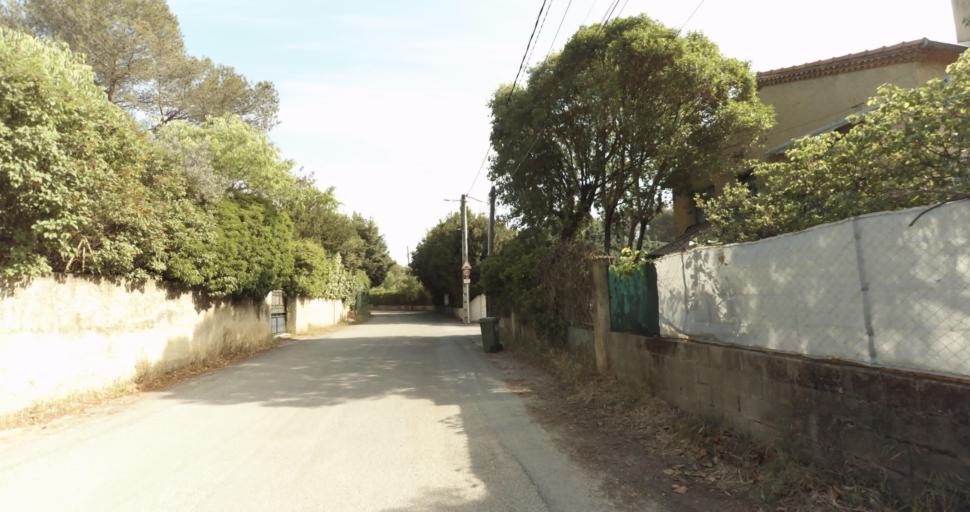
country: FR
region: Languedoc-Roussillon
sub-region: Departement du Gard
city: Nimes
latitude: 43.8583
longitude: 4.3821
